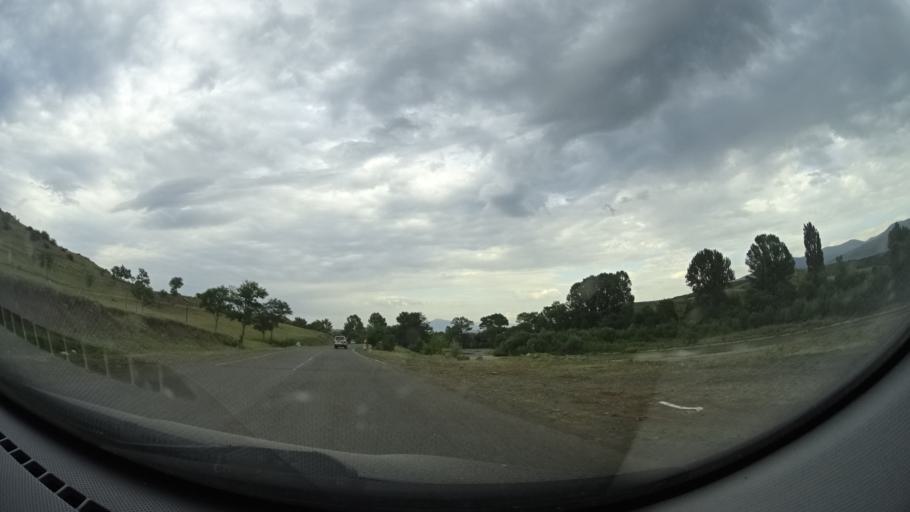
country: GE
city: Vale
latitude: 41.6467
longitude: 42.8570
